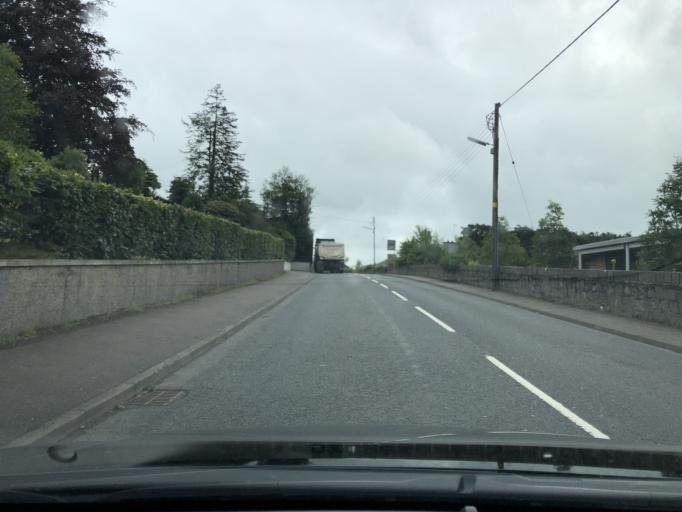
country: GB
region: Northern Ireland
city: Ballynahinch
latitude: 54.3986
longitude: -5.8959
